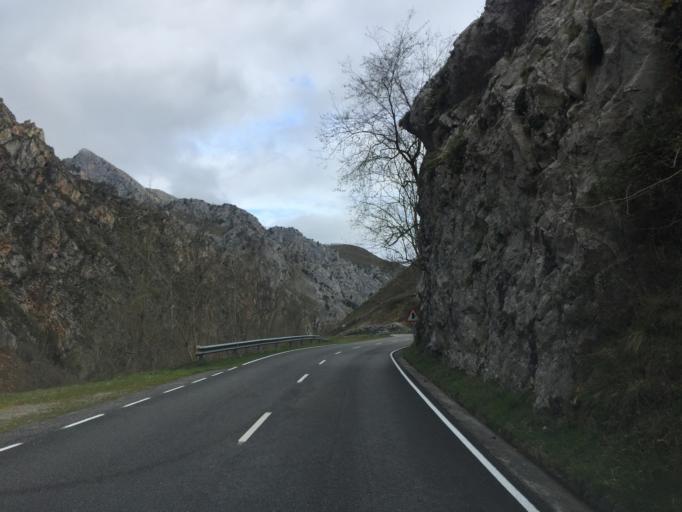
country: ES
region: Asturias
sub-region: Province of Asturias
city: Carrena
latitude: 43.2732
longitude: -4.8329
